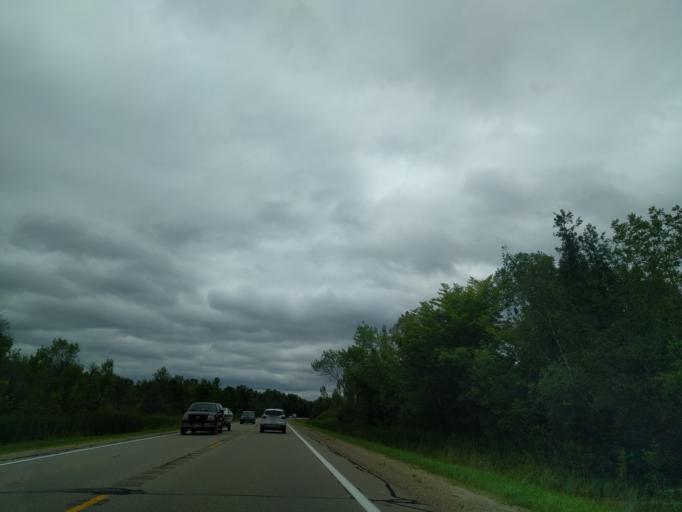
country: US
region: Michigan
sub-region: Menominee County
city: Menominee
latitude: 45.3834
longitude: -87.3750
